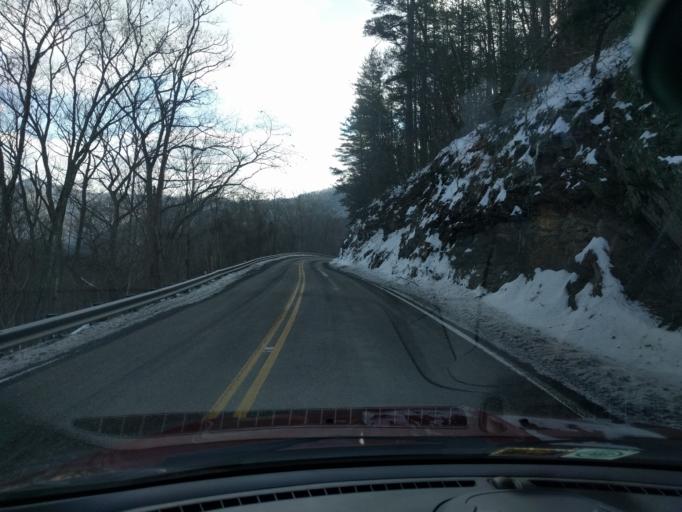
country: US
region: Virginia
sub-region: Bath County
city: Warm Springs
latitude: 38.1231
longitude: -79.9430
